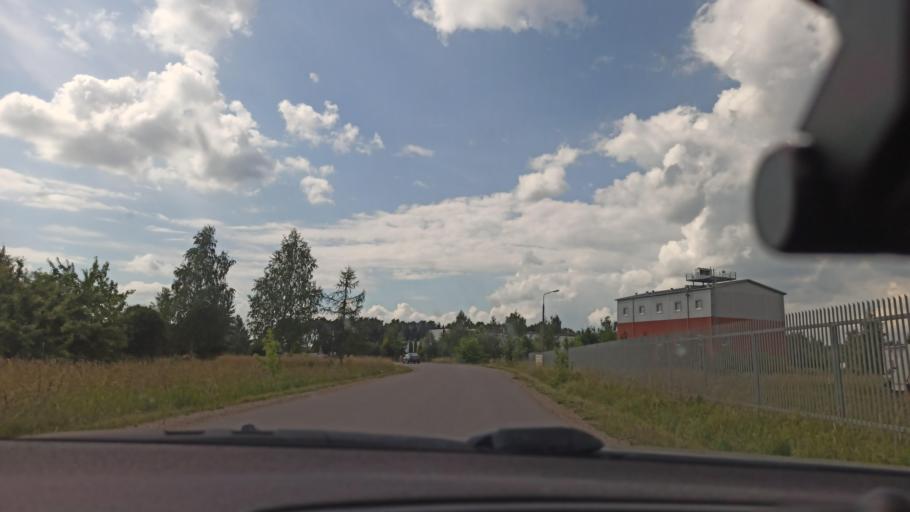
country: PL
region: Podlasie
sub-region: Powiat bialostocki
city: Turosn Koscielna
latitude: 53.0678
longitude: 23.0884
